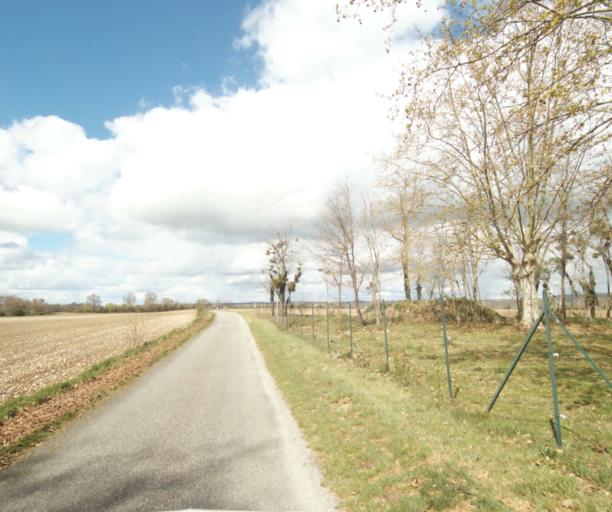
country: FR
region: Midi-Pyrenees
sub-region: Departement de l'Ariege
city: Saverdun
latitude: 43.2718
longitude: 1.5814
